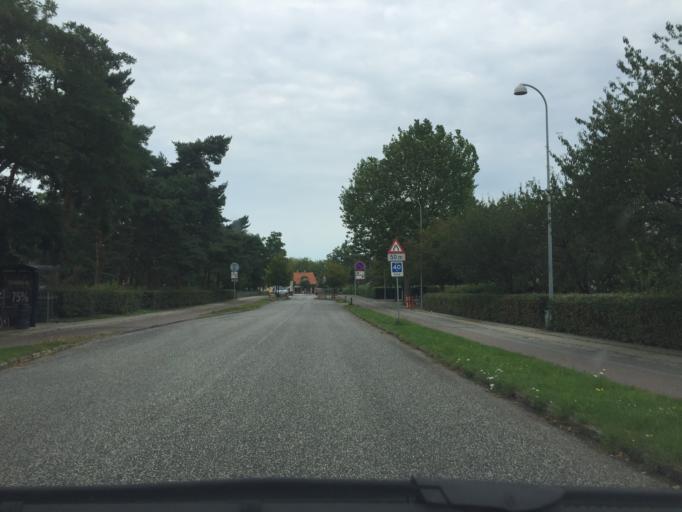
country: DK
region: Capital Region
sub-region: Lyngby-Tarbaek Kommune
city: Kongens Lyngby
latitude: 55.7951
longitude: 12.5225
